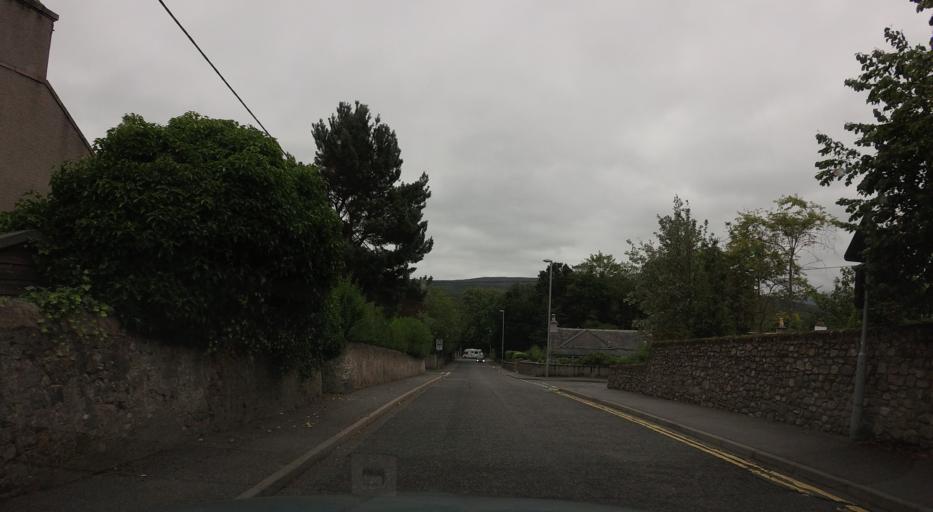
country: GB
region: Scotland
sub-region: Aberdeenshire
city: Banchory
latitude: 57.0524
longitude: -2.4939
